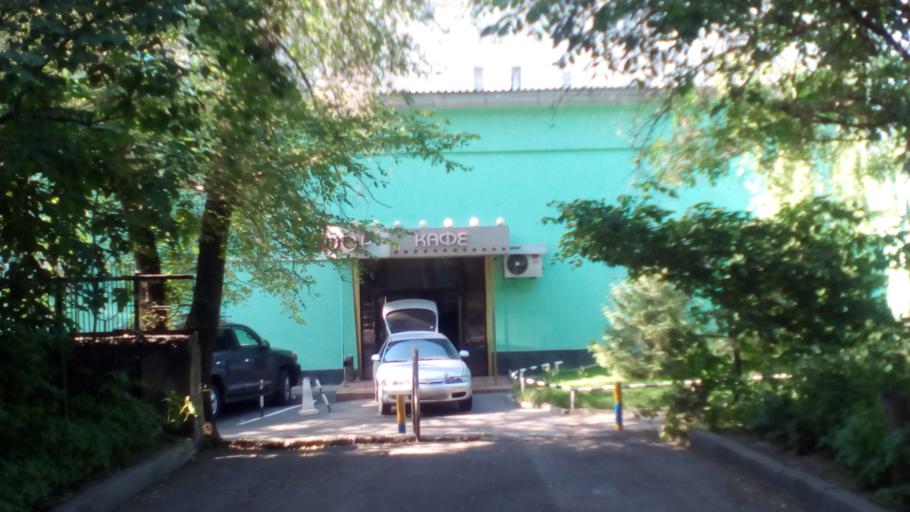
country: KZ
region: Almaty Qalasy
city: Almaty
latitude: 43.2482
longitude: 76.9394
